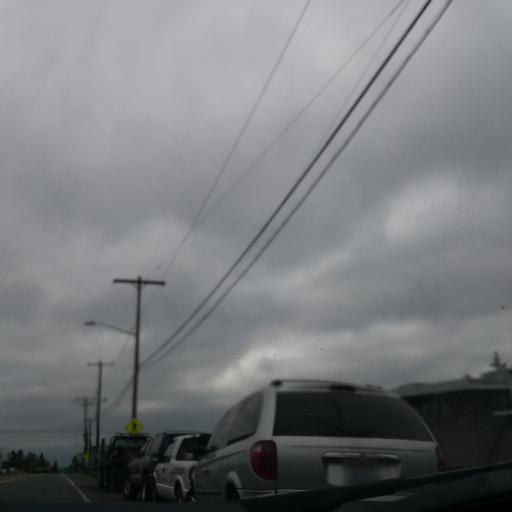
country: US
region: Washington
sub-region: King County
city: White Center
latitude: 47.5066
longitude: -122.3337
